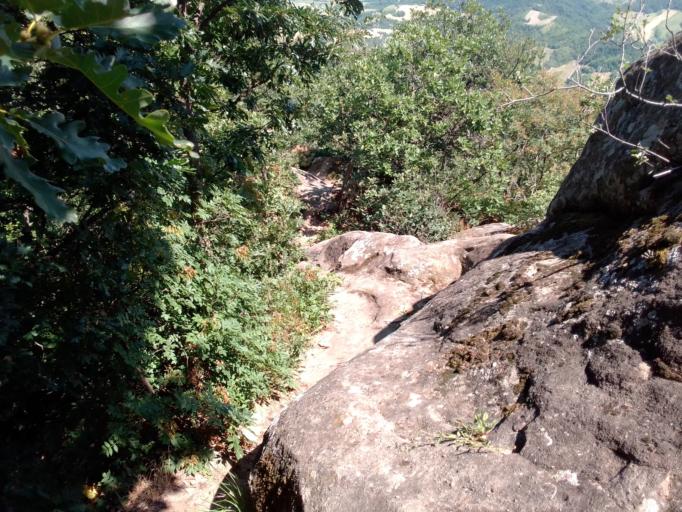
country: IT
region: Emilia-Romagna
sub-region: Provincia di Piacenza
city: Pianello Val Tidone
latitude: 44.9160
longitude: 9.3999
